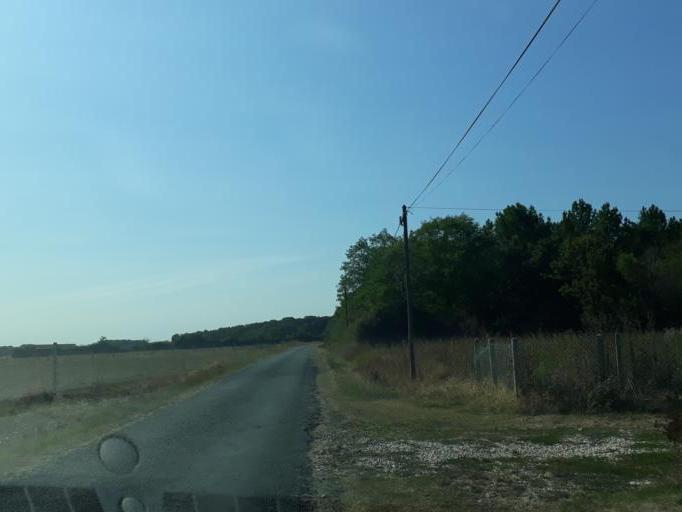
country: FR
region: Centre
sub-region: Departement de l'Indre
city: Chabris
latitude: 47.2609
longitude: 1.6388
